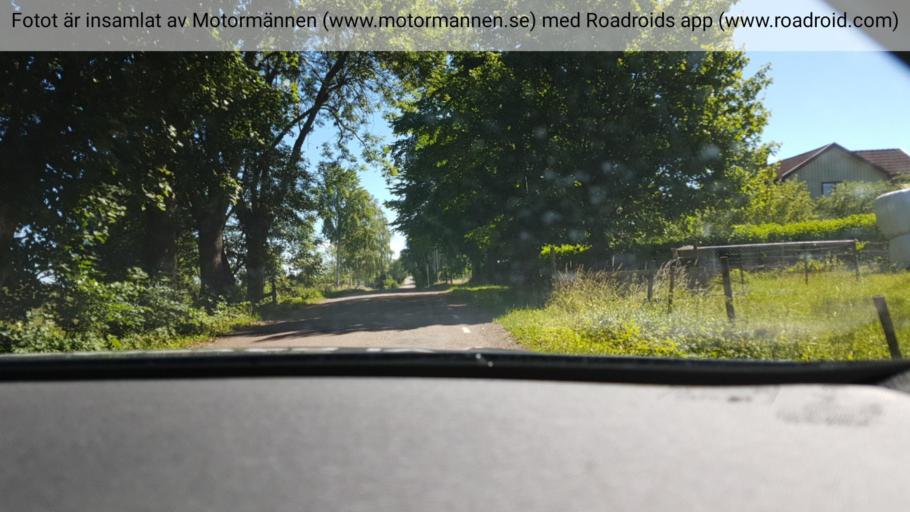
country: SE
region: Vaestra Goetaland
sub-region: Falkopings Kommun
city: Akarp
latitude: 58.2483
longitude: 13.7540
